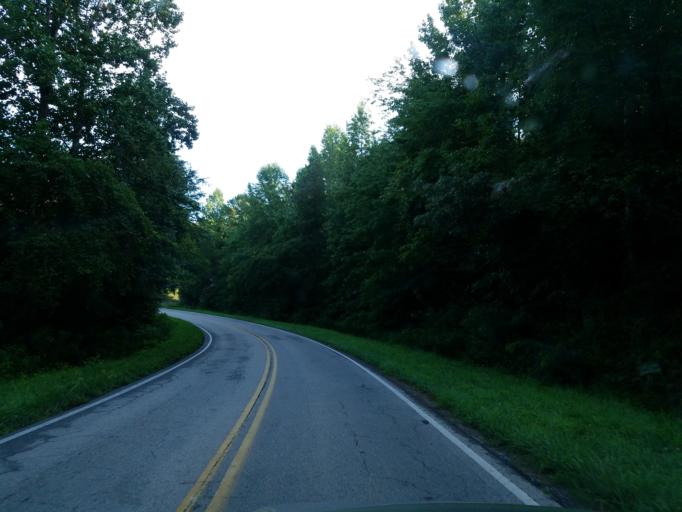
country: US
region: Georgia
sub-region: Lumpkin County
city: Dahlonega
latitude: 34.5539
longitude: -83.8857
